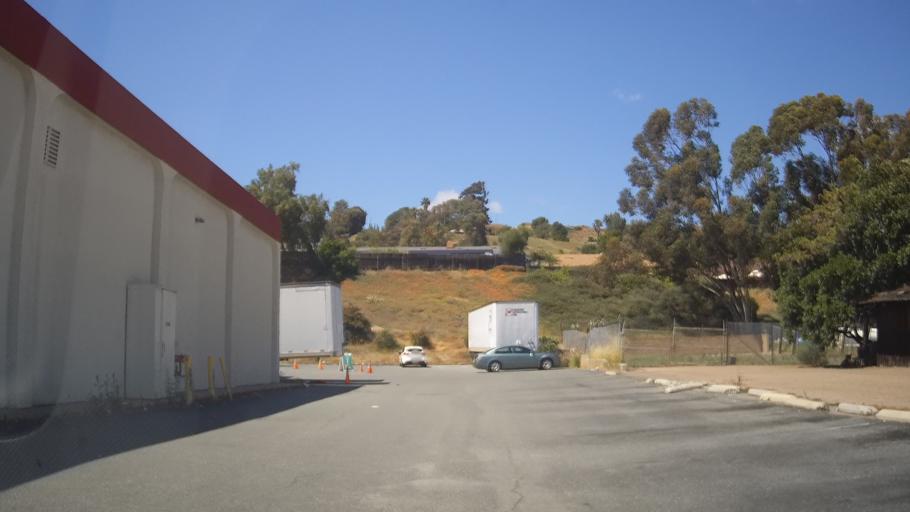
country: US
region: California
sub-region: San Diego County
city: Poway
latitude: 32.9539
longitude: -117.0492
